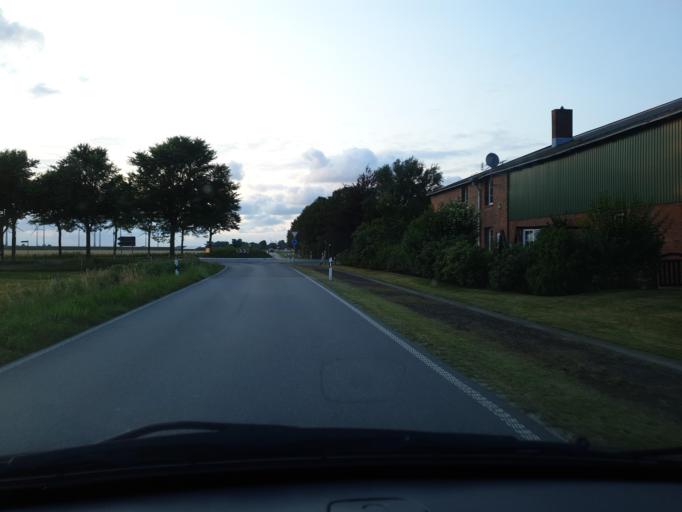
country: DE
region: Schleswig-Holstein
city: Kronprinzenkoog
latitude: 53.9463
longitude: 8.9406
